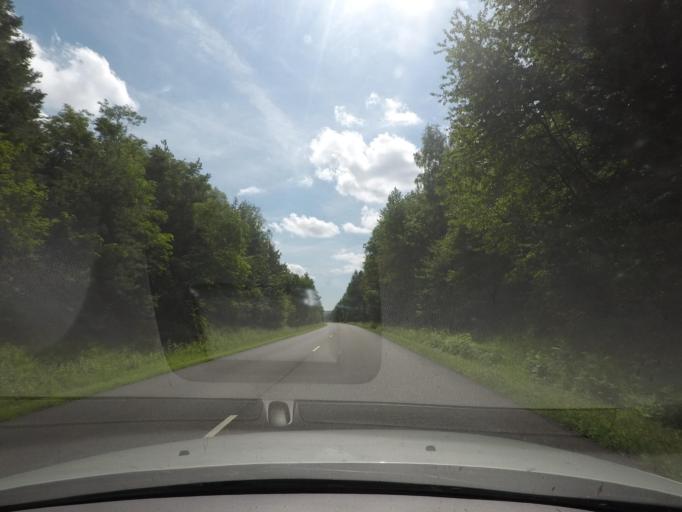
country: FR
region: Alsace
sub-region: Departement du Bas-Rhin
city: Drulingen
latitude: 48.8729
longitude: 7.1641
